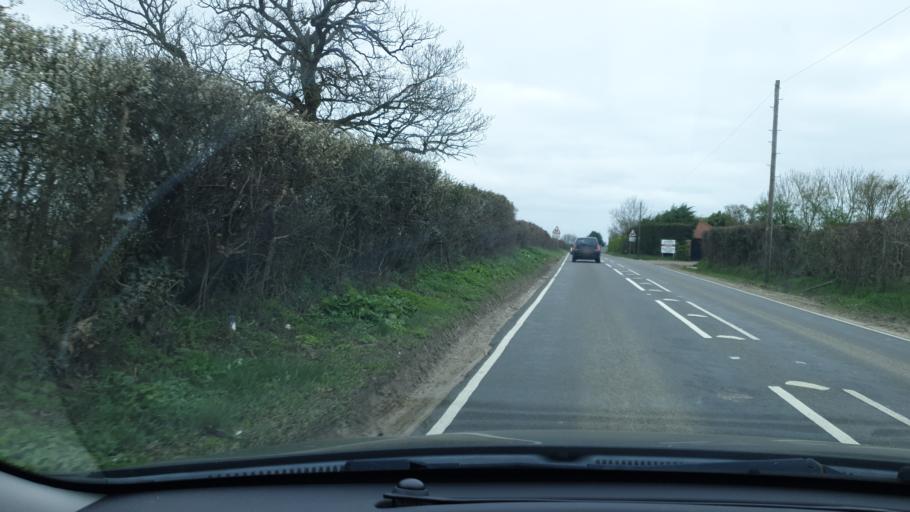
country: GB
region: England
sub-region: Essex
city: Great Horkesley
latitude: 51.9566
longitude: 0.8709
